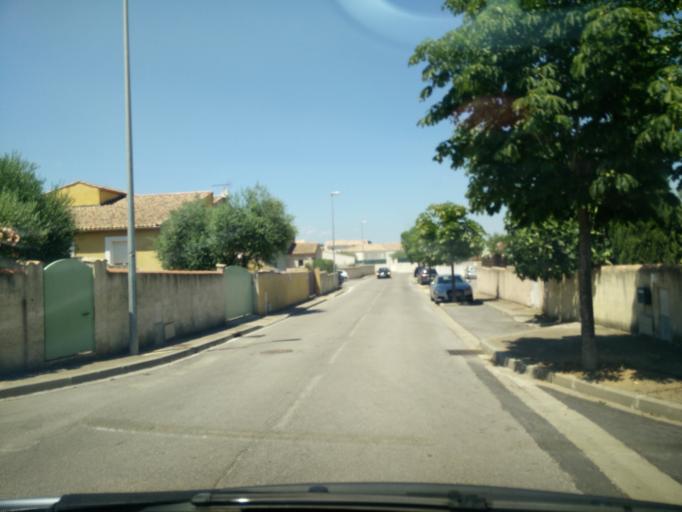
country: FR
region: Languedoc-Roussillon
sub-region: Departement de l'Herault
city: Villetelle
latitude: 43.7203
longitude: 4.1090
